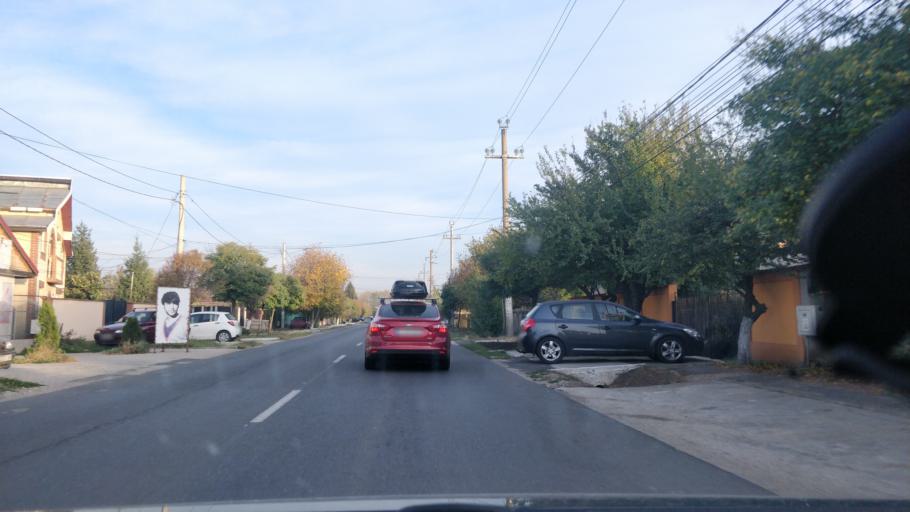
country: RO
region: Ilfov
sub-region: Comuna Ciorogarla
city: Ciorogarla
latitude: 44.4437
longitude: 25.8702
